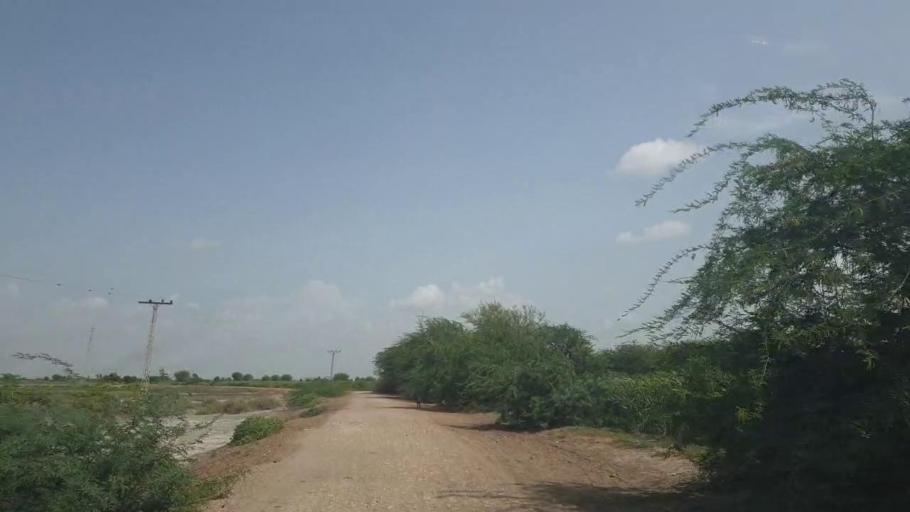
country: PK
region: Sindh
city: Tando Bago
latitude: 24.7577
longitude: 69.1695
